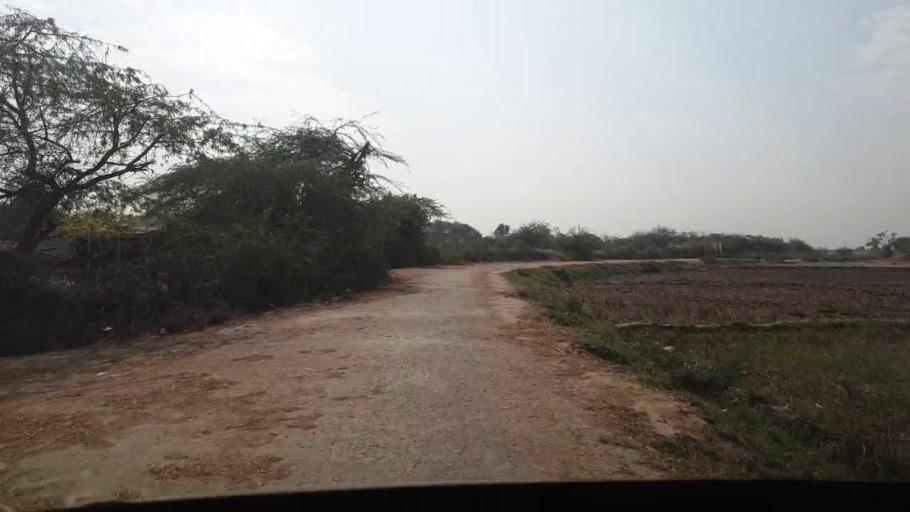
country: PK
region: Sindh
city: Chuhar Jamali
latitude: 24.3167
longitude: 67.9444
